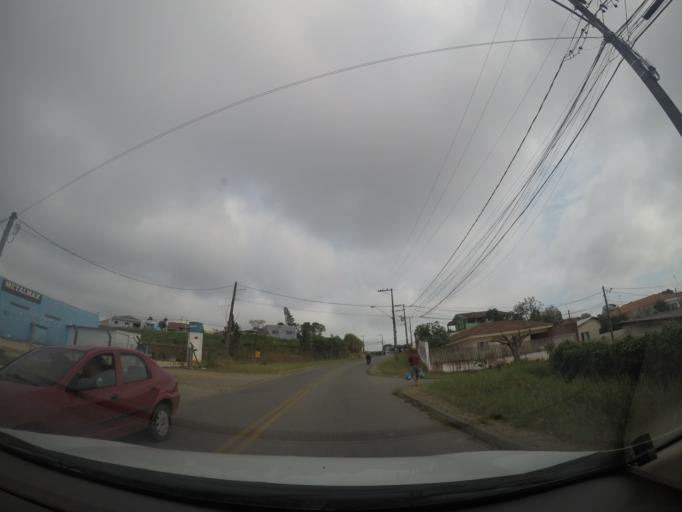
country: BR
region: Parana
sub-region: Colombo
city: Colombo
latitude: -25.3481
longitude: -49.2166
